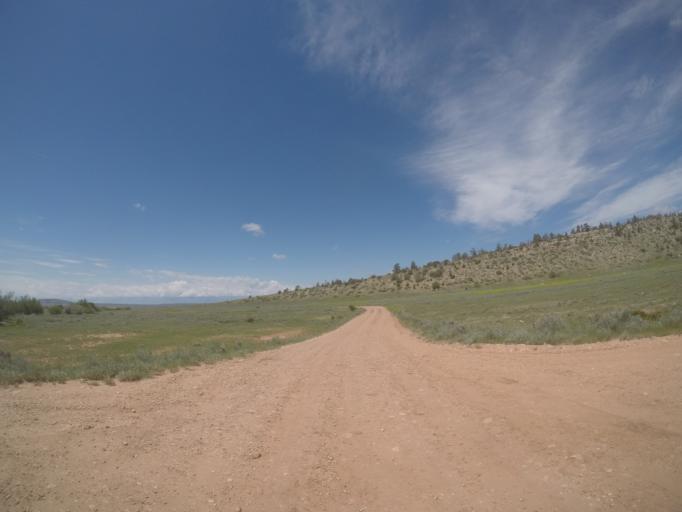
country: US
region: Montana
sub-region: Yellowstone County
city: Laurel
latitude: 45.2402
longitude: -108.6715
